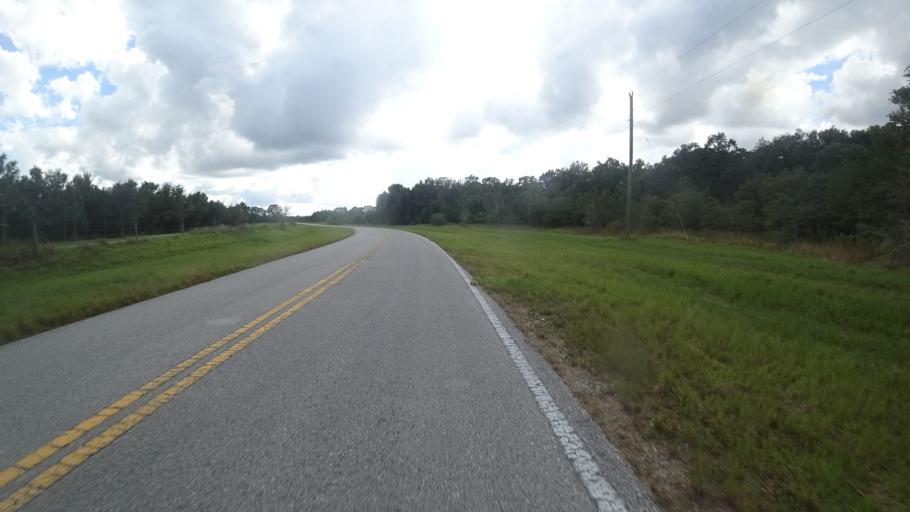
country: US
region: Florida
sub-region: Hillsborough County
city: Wimauma
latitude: 27.5867
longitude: -82.1816
